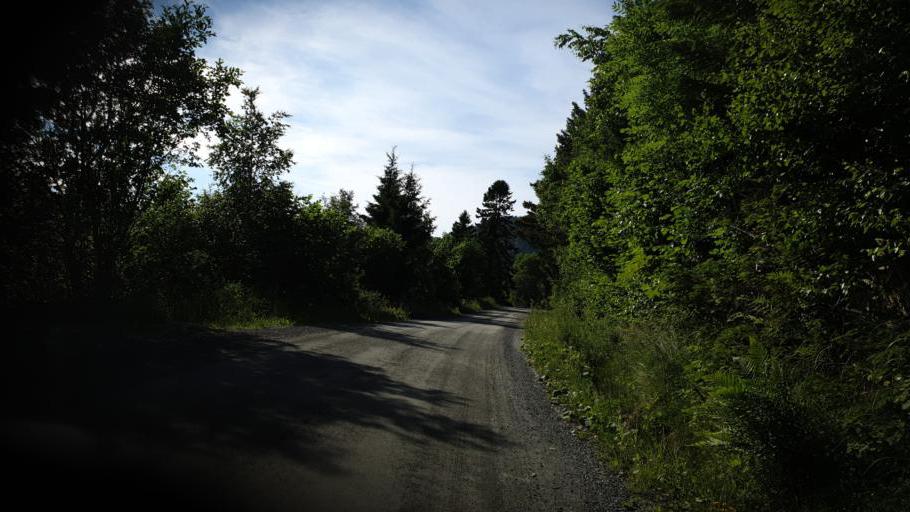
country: NO
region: Sor-Trondelag
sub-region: Trondheim
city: Trondheim
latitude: 63.5736
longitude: 10.3974
